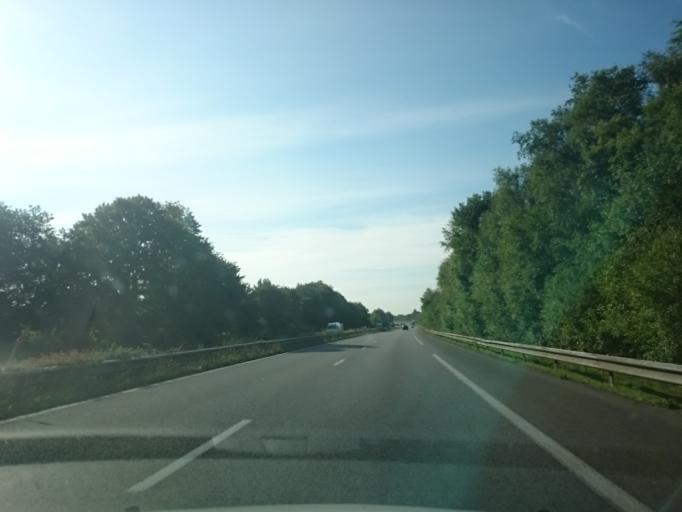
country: FR
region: Brittany
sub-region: Departement du Finistere
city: Saint-Yvi
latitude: 47.9563
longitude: -3.9514
